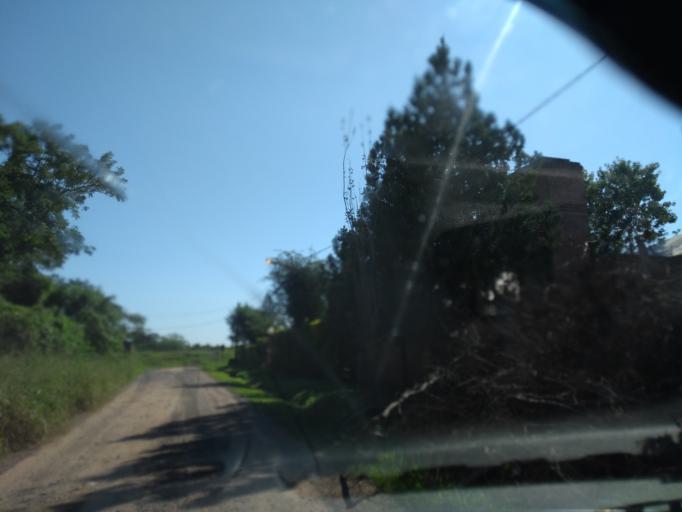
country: AR
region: Chaco
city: Barranqueras
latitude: -27.4378
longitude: -58.9099
